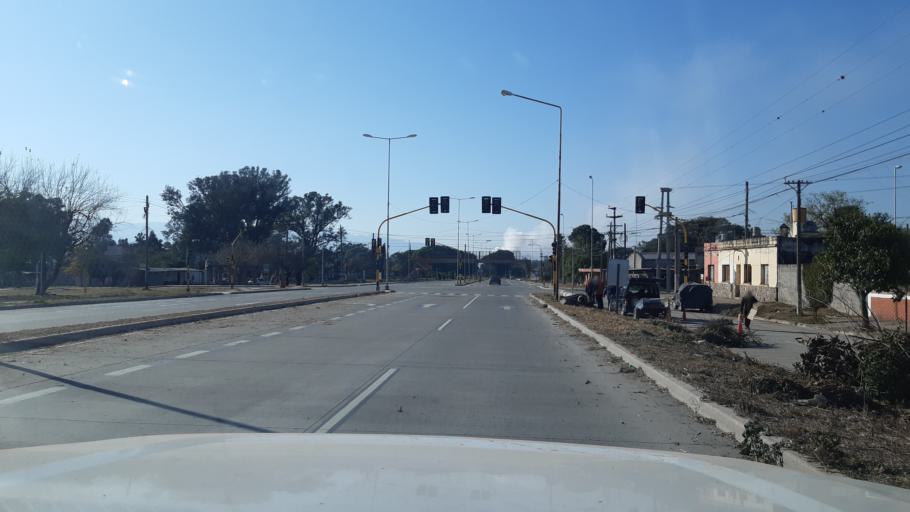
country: AR
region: Jujuy
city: Palpala
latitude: -24.2266
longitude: -65.2388
